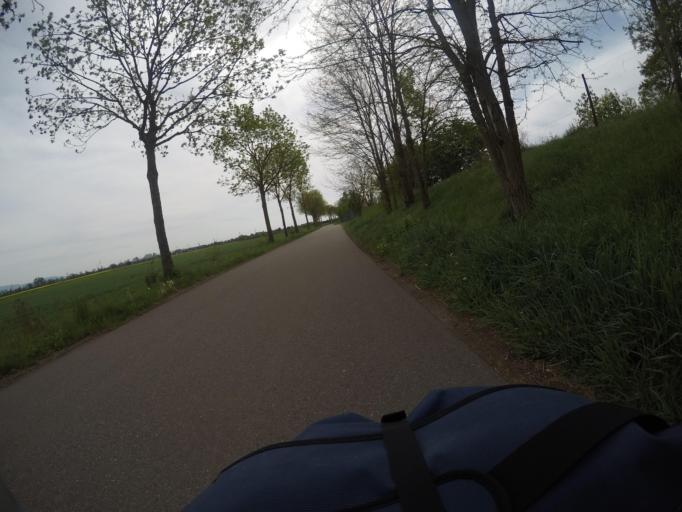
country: DE
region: Baden-Wuerttemberg
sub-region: Freiburg Region
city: Kehl
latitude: 48.5868
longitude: 7.8405
